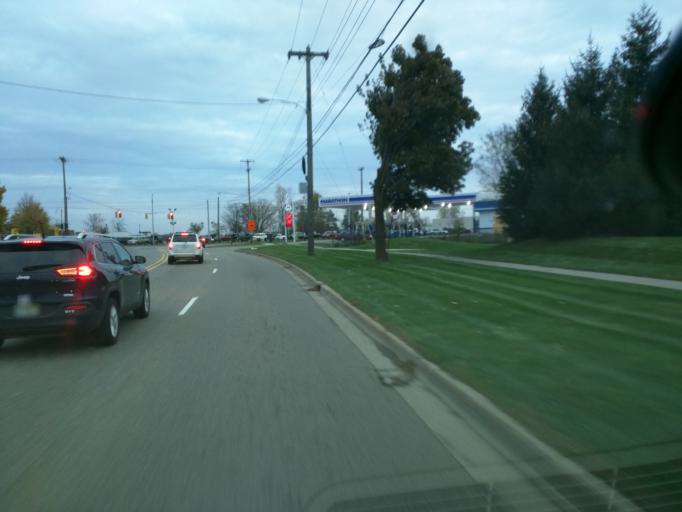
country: US
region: Michigan
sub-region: Ingham County
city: Edgemont Park
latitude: 42.7686
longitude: -84.6011
